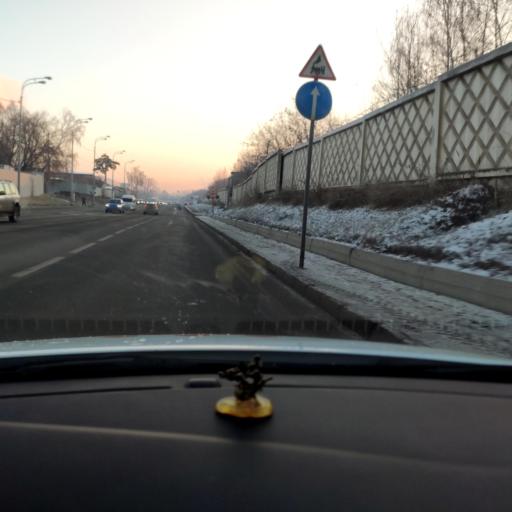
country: RU
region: Tatarstan
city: Staroye Arakchino
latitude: 55.8379
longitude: 49.0439
